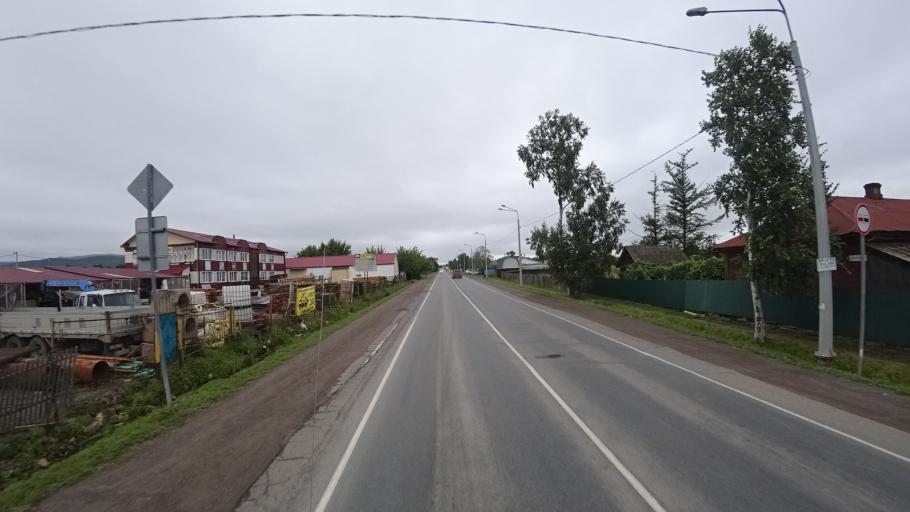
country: RU
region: Primorskiy
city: Chernigovka
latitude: 44.3358
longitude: 132.5825
